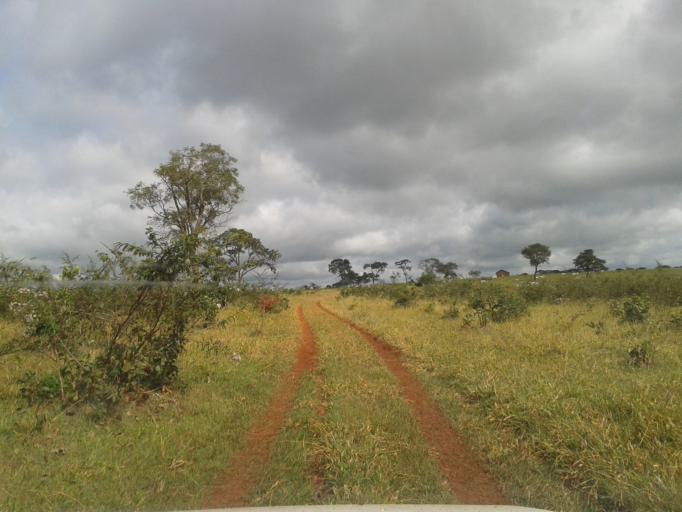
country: BR
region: Minas Gerais
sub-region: Campina Verde
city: Campina Verde
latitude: -19.4145
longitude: -49.6755
